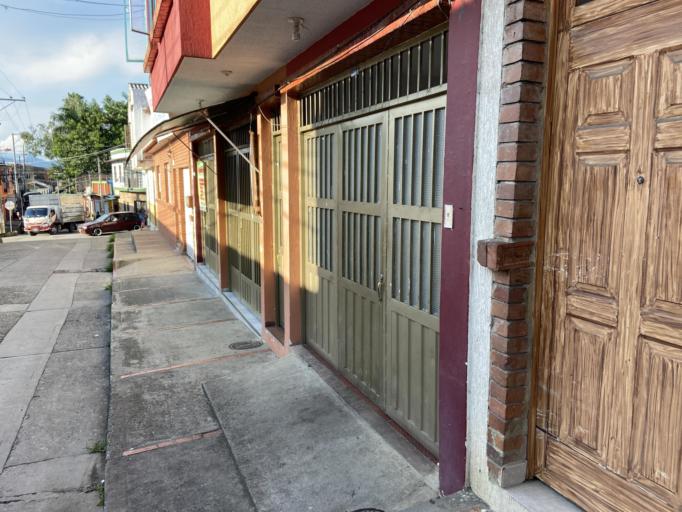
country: CO
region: Cundinamarca
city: San Antonio del Tequendama
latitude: 4.6306
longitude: -74.4612
